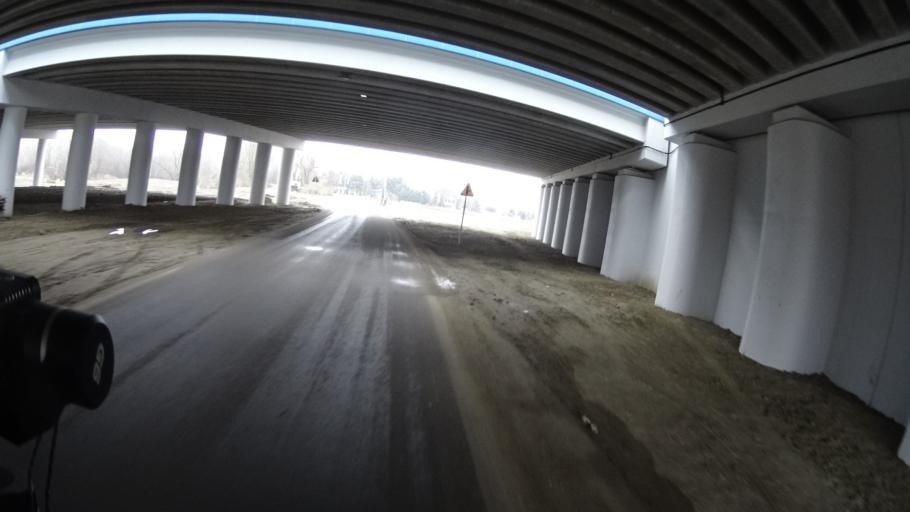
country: PL
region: Masovian Voivodeship
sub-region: Warszawa
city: Wilanow
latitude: 52.1526
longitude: 21.1120
